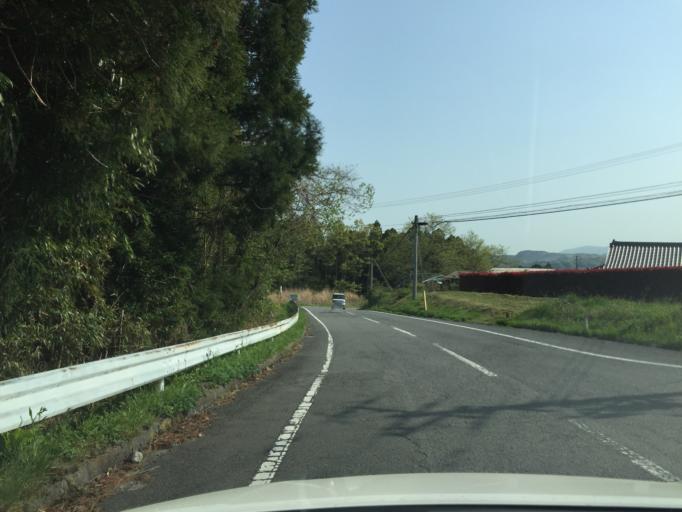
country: JP
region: Fukushima
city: Iwaki
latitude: 37.1499
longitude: 140.8585
